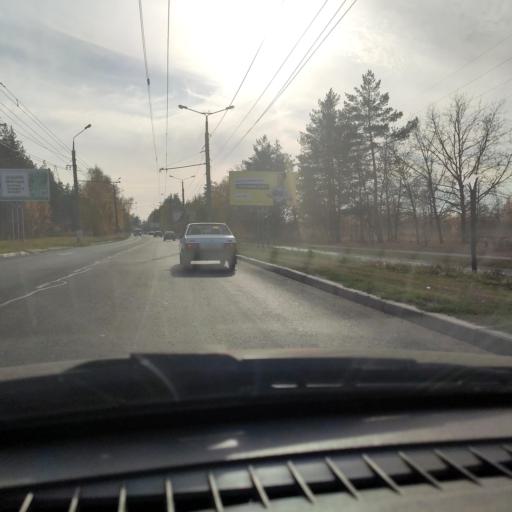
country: RU
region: Samara
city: Tol'yatti
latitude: 53.4952
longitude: 49.3868
